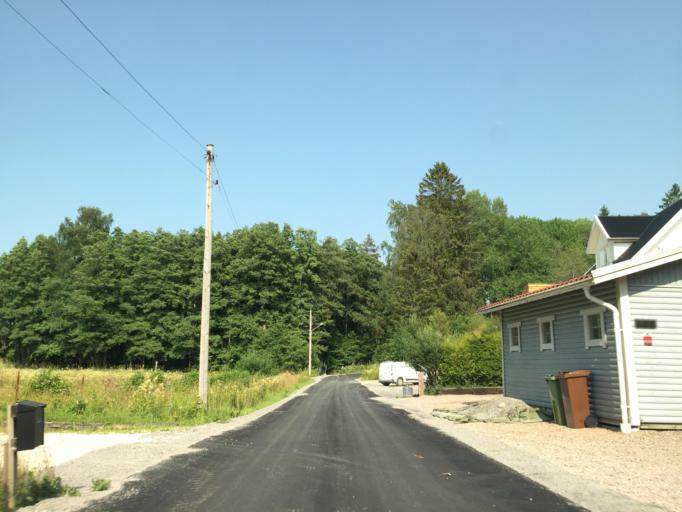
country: SE
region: Vaestra Goetaland
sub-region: Vanersborgs Kommun
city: Vanersborg
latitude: 58.3672
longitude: 12.2941
